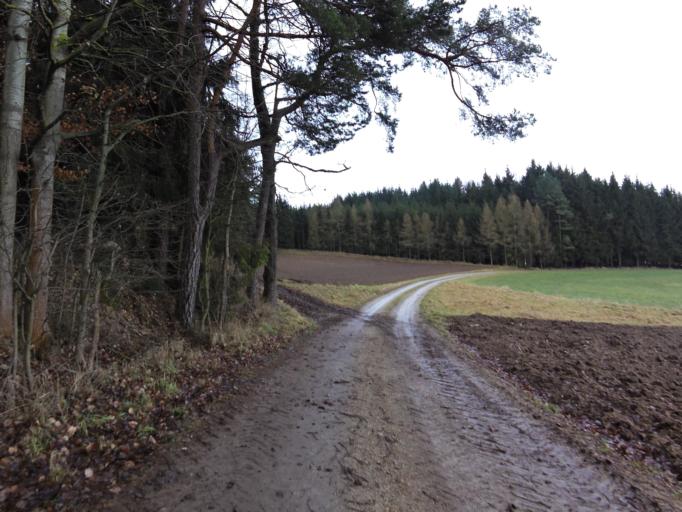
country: DE
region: Bavaria
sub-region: Upper Franconia
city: Wunsiedel
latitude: 50.0662
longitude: 12.0340
